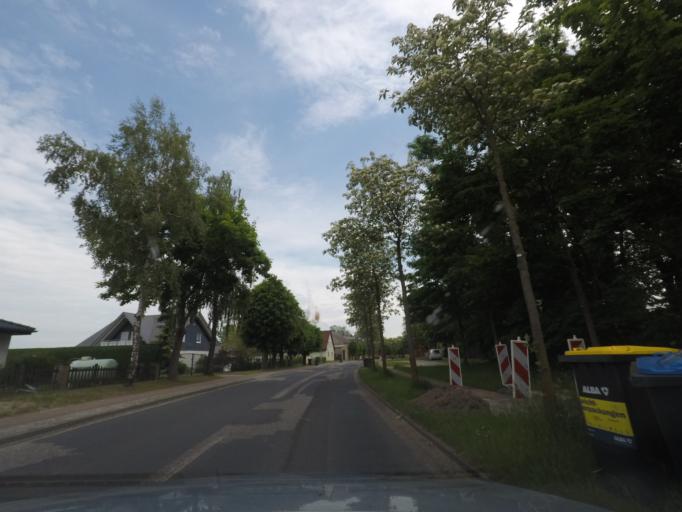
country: DE
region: Brandenburg
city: Schenkenberg
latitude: 53.3463
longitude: 13.9481
